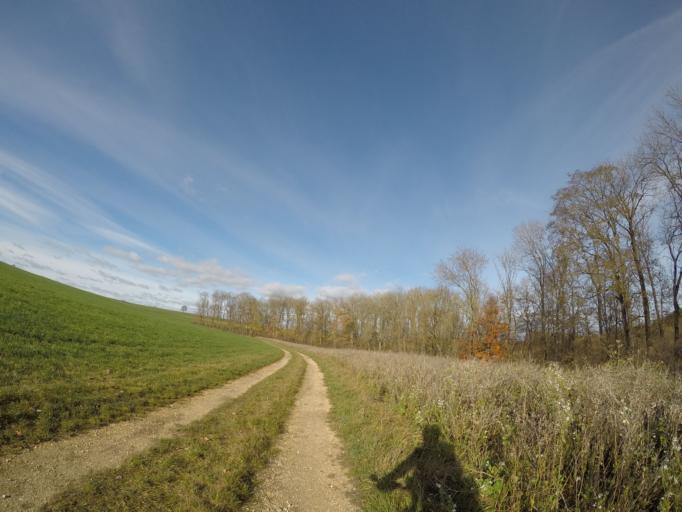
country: DE
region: Baden-Wuerttemberg
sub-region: Tuebingen Region
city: Dornstadt
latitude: 48.4443
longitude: 9.9351
